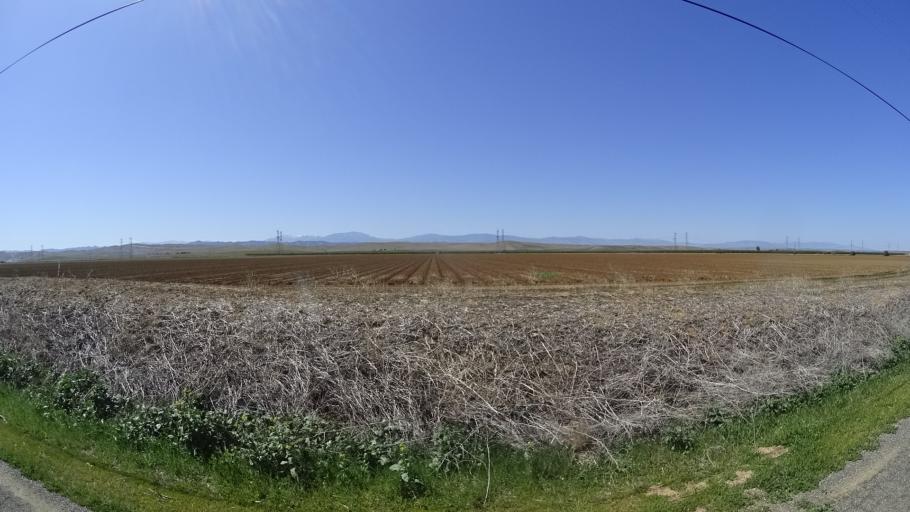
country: US
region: California
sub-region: Glenn County
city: Willows
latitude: 39.4911
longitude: -122.2773
